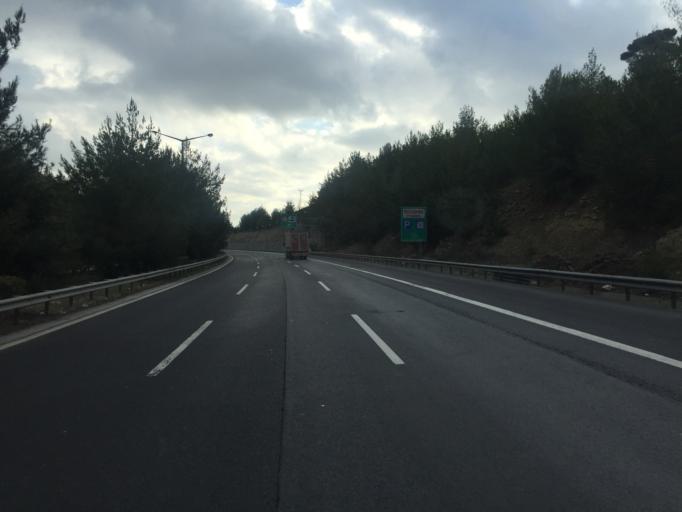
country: TR
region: Mersin
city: Camliyayla
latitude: 37.1975
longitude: 34.8266
